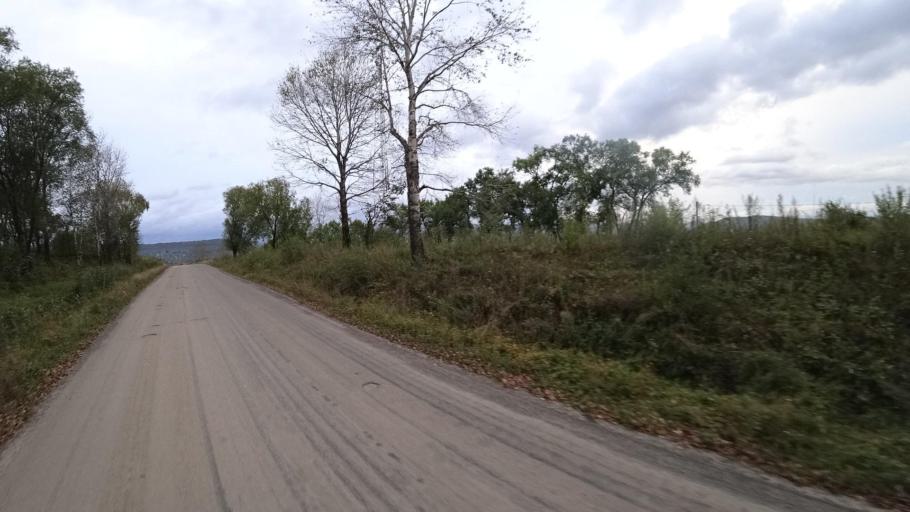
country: RU
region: Jewish Autonomous Oblast
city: Izvestkovyy
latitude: 48.9762
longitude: 131.5706
